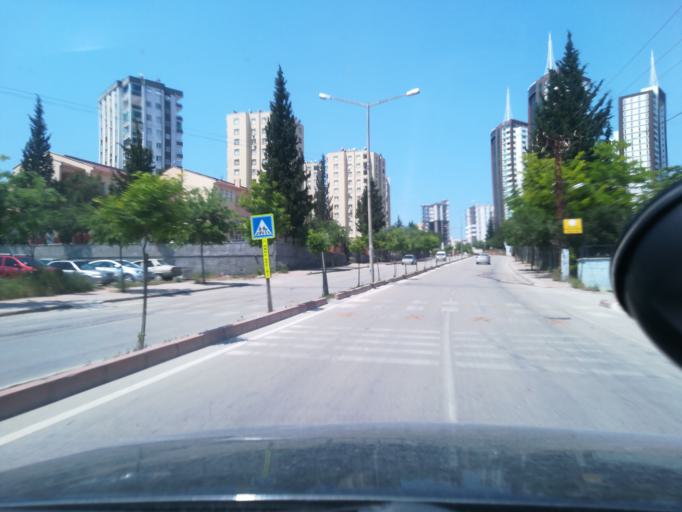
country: TR
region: Adana
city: Seyhan
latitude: 37.0337
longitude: 35.2668
